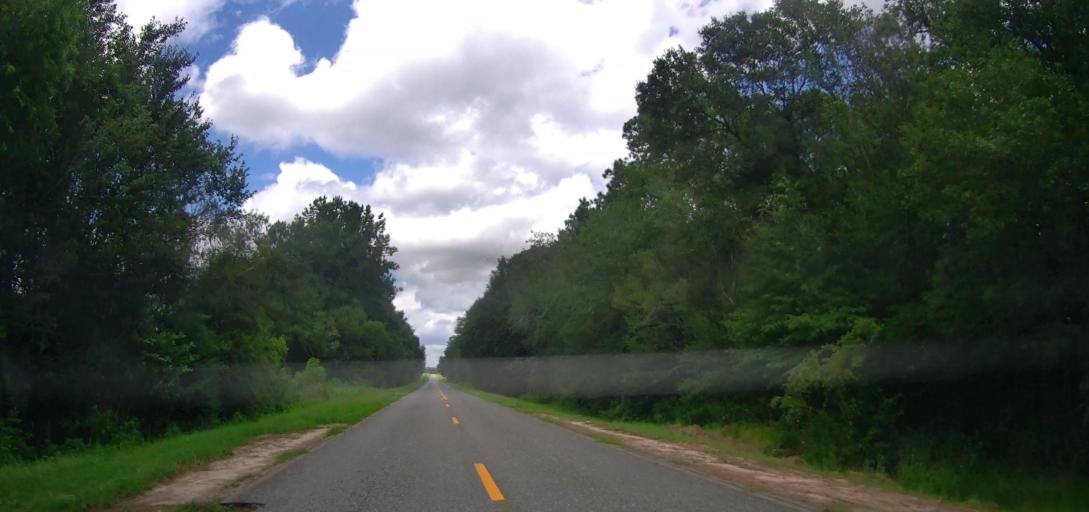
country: US
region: Georgia
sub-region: Turner County
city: Ashburn
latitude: 31.7171
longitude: -83.5055
